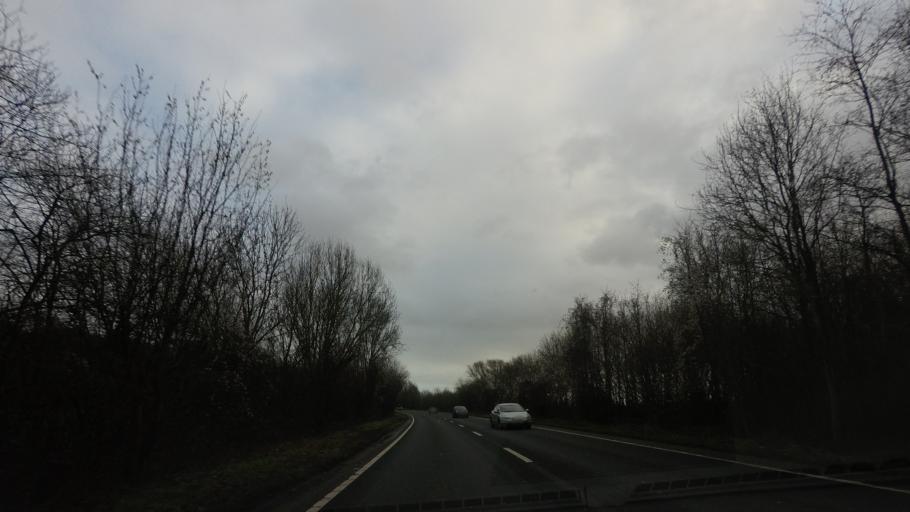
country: GB
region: England
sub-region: Kent
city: East Peckham
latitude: 51.2271
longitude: 0.3900
